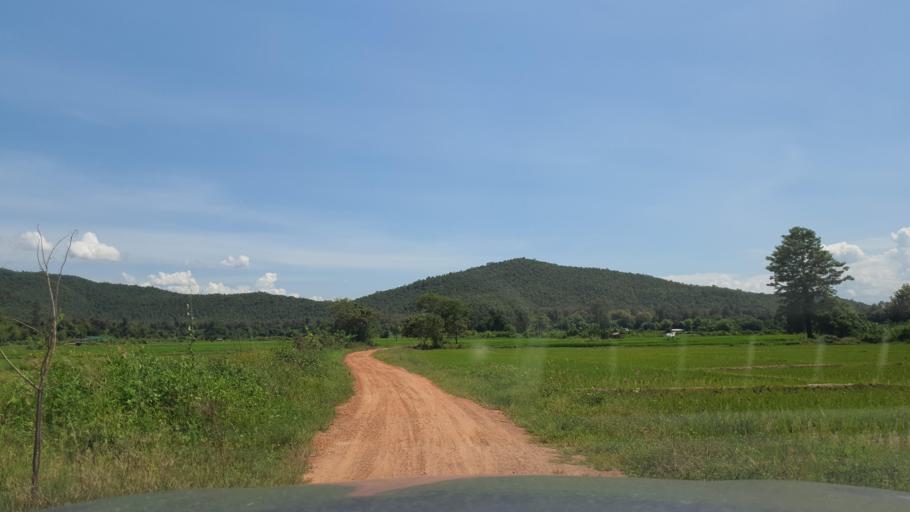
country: TH
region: Chiang Mai
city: Mae On
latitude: 18.7837
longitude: 99.1878
